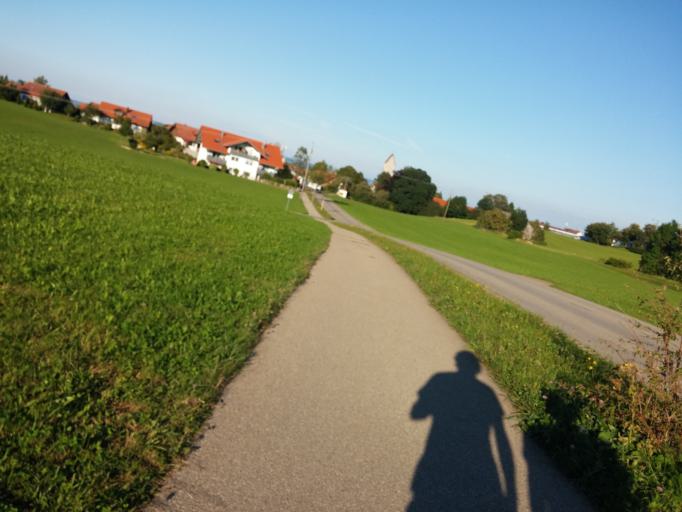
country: DE
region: Bavaria
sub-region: Swabia
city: Wiggensbach
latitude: 47.7453
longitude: 10.2258
